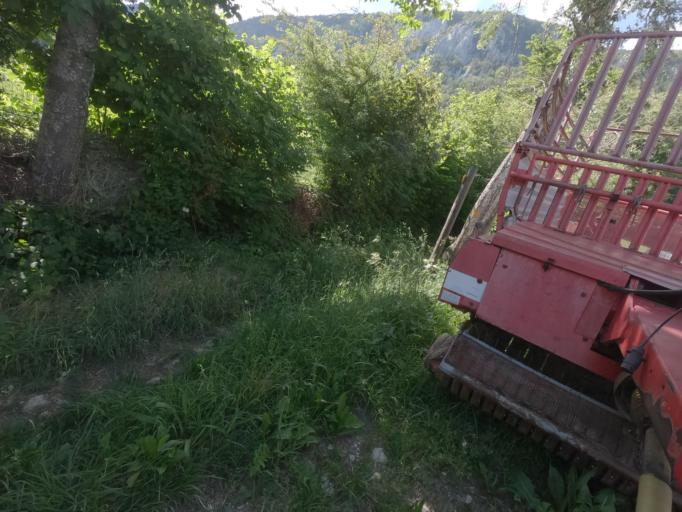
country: CH
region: Solothurn
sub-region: Bezirk Lebern
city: Langendorf
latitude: 47.2412
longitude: 7.5307
